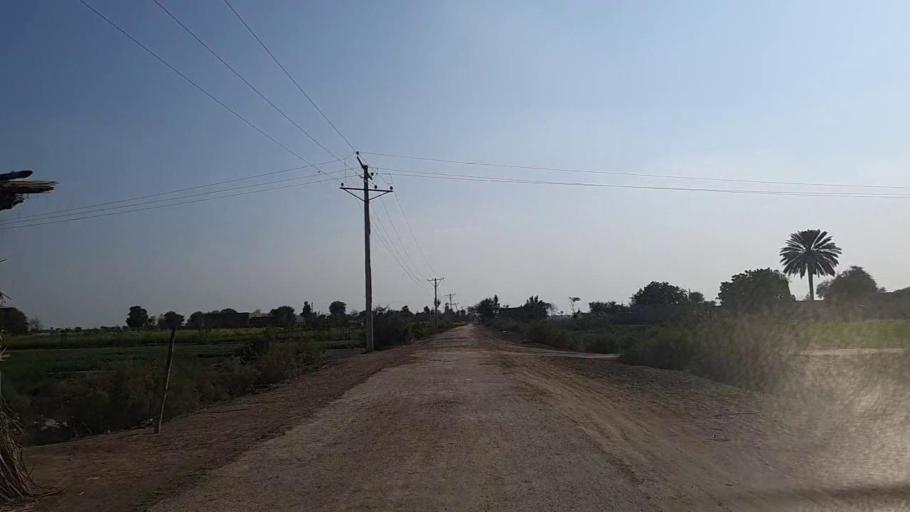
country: PK
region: Sindh
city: Jam Sahib
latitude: 26.2793
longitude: 68.6046
